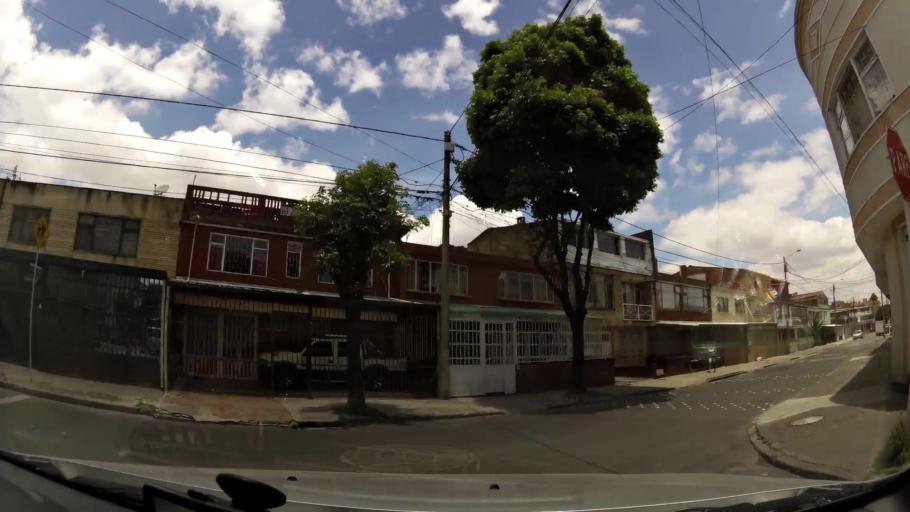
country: CO
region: Bogota D.C.
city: Bogota
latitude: 4.5957
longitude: -74.0926
